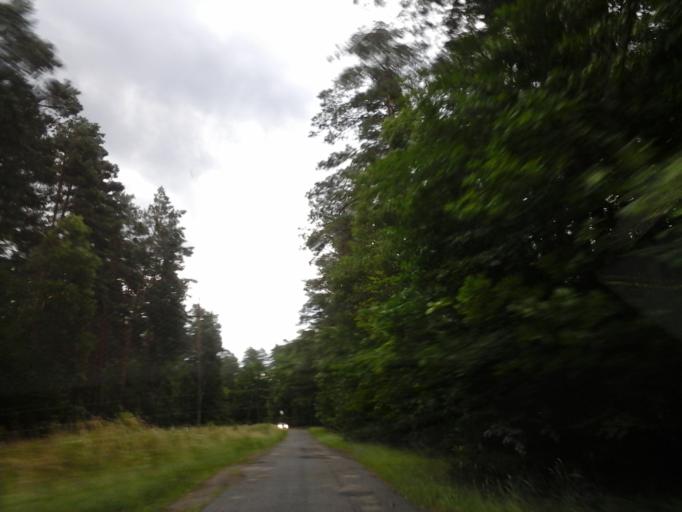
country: PL
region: West Pomeranian Voivodeship
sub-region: Powiat drawski
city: Kalisz Pomorski
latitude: 53.1541
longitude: 15.8984
